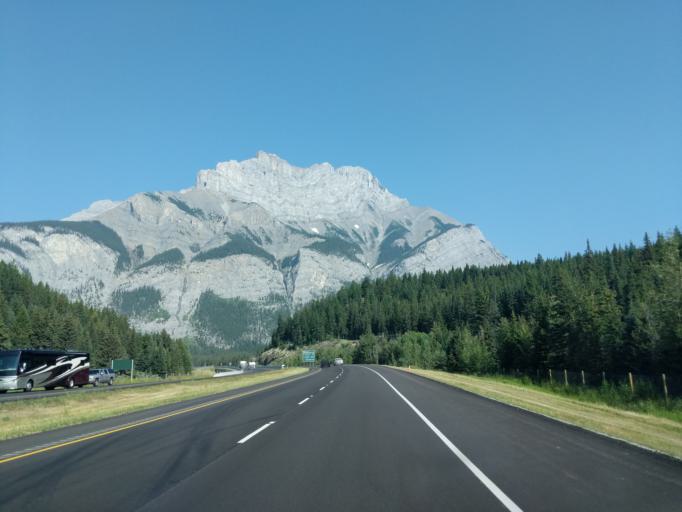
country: CA
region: Alberta
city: Banff
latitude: 51.2046
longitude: -115.5211
